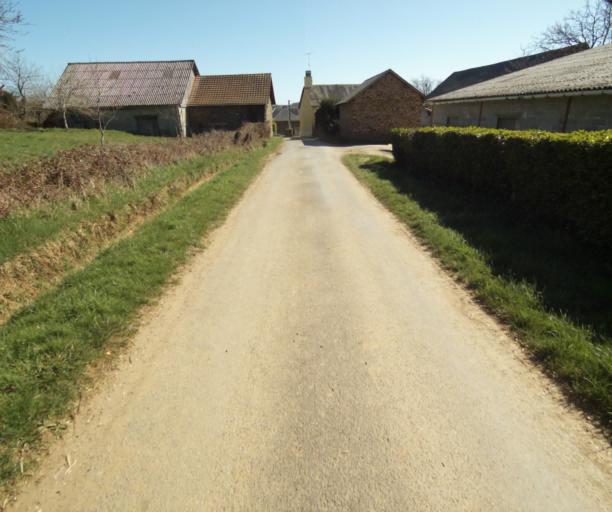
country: FR
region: Limousin
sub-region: Departement de la Correze
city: Uzerche
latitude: 45.4136
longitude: 1.6308
